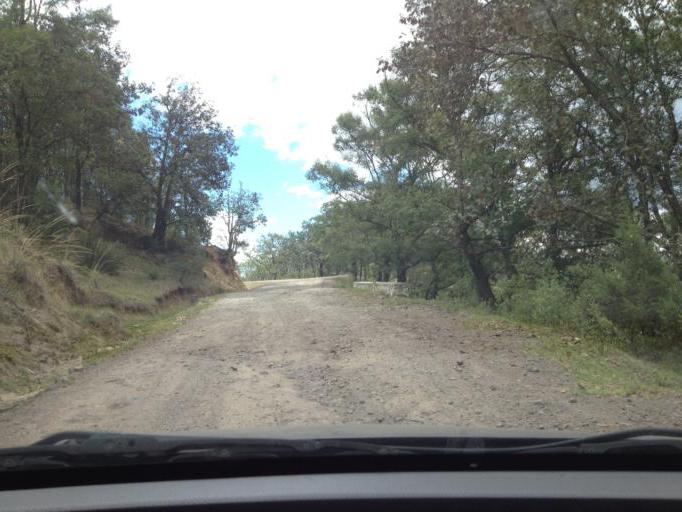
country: MX
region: Hidalgo
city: Mineral del Monte
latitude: 20.2082
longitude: -98.6740
